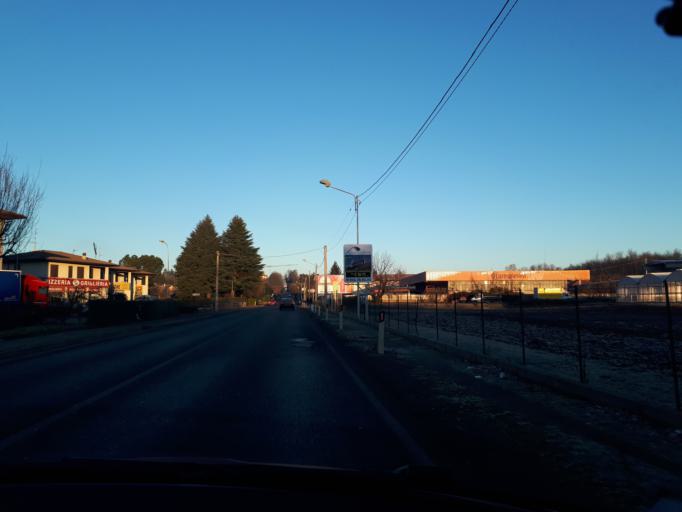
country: IT
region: Lombardy
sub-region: Provincia di Como
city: Cermenate
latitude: 45.7057
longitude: 9.0895
